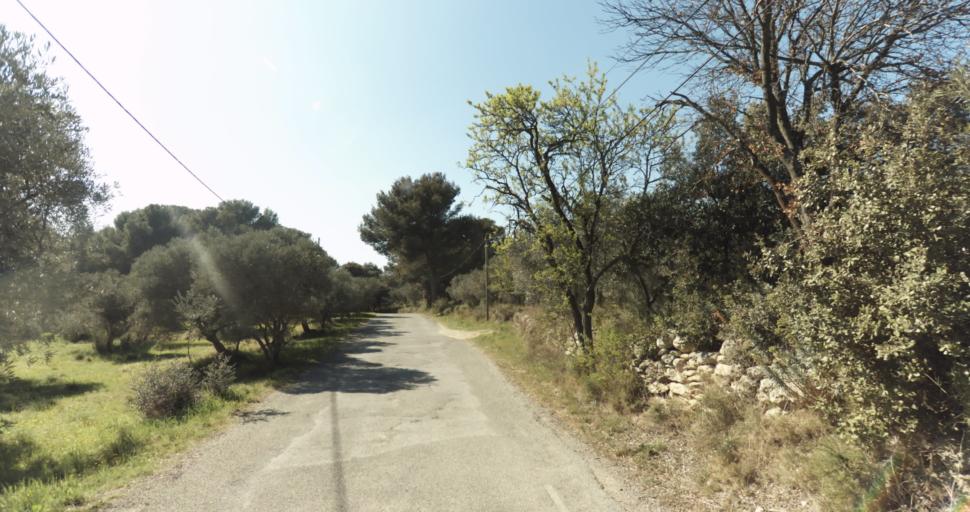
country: FR
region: Provence-Alpes-Cote d'Azur
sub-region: Departement des Bouches-du-Rhone
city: Pelissanne
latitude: 43.6447
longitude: 5.1792
